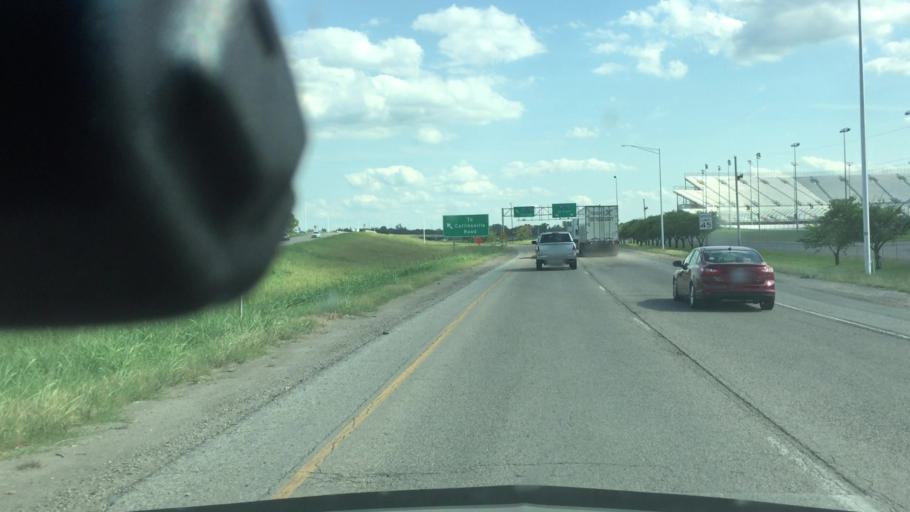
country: US
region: Illinois
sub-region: Saint Clair County
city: East Saint Louis
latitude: 38.6512
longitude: -90.1329
